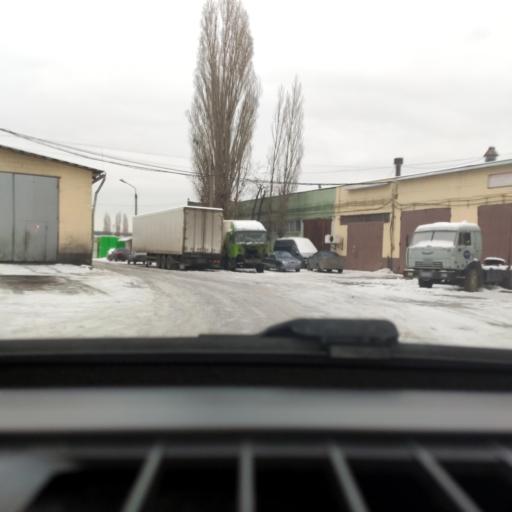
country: RU
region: Voronezj
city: Voronezh
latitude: 51.6697
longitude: 39.1381
